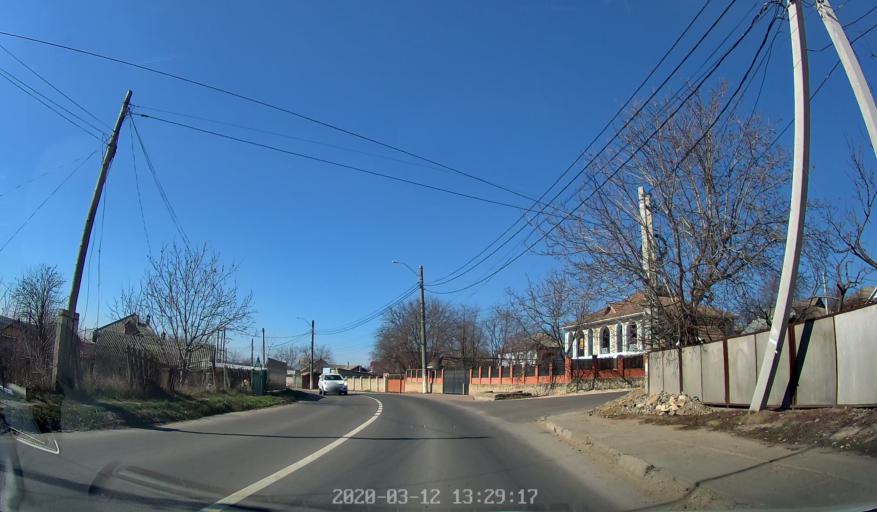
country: MD
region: Laloveni
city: Ialoveni
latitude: 46.9422
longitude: 28.7833
